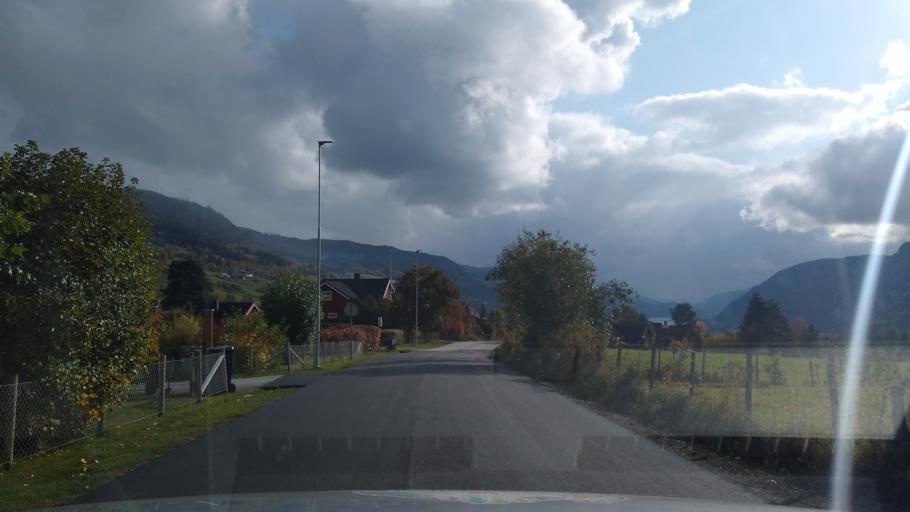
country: NO
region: Oppland
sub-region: Ringebu
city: Ringebu
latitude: 61.5376
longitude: 10.1359
